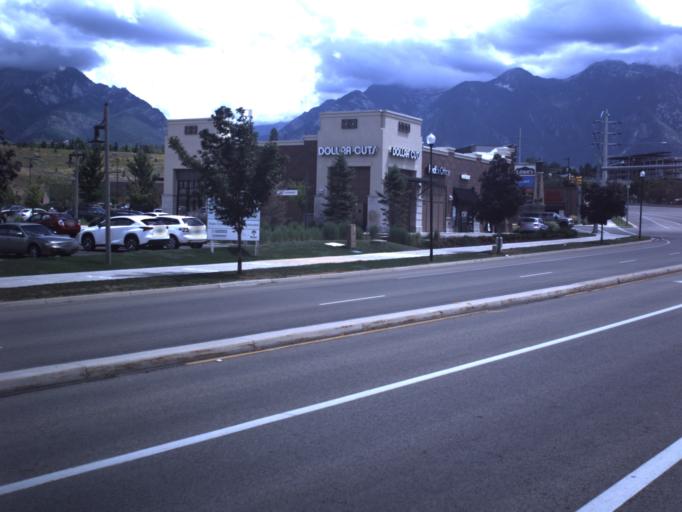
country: US
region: Utah
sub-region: Salt Lake County
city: Sandy Hills
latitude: 40.5817
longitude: -111.8624
